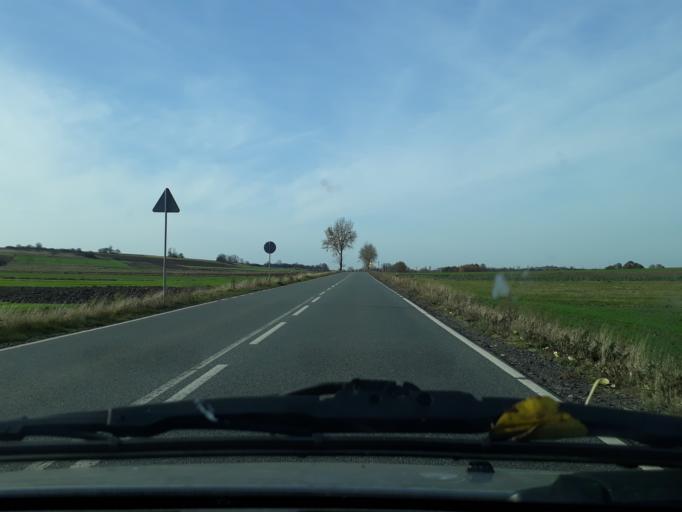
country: PL
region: Silesian Voivodeship
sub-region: Powiat myszkowski
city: Gniazdow
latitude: 50.5902
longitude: 19.0950
